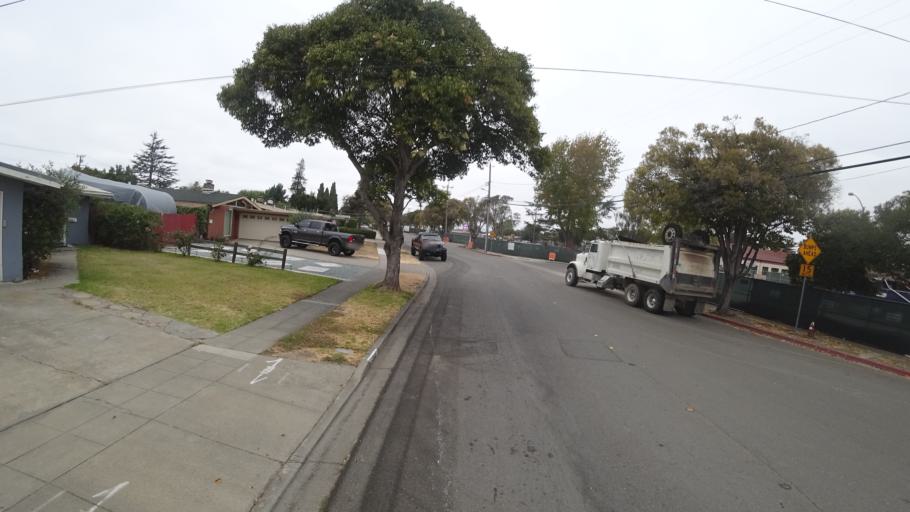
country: US
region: California
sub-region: Alameda County
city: Hayward
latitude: 37.6463
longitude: -122.0984
